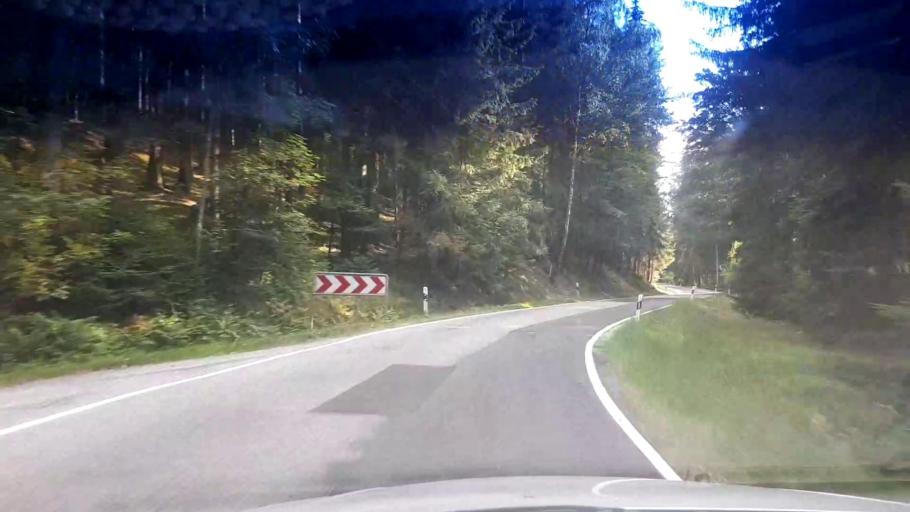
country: DE
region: Bavaria
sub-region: Upper Palatinate
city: Neualbenreuth
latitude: 49.9238
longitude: 12.4059
